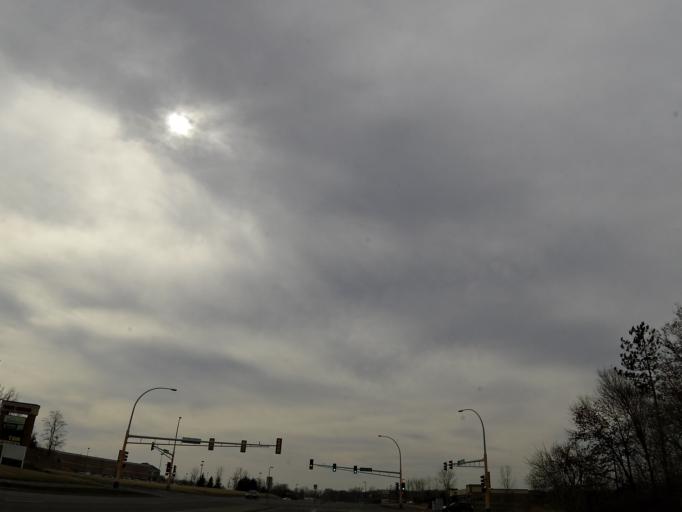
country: US
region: Minnesota
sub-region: Dakota County
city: Inver Grove Heights
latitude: 44.8196
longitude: -93.0390
